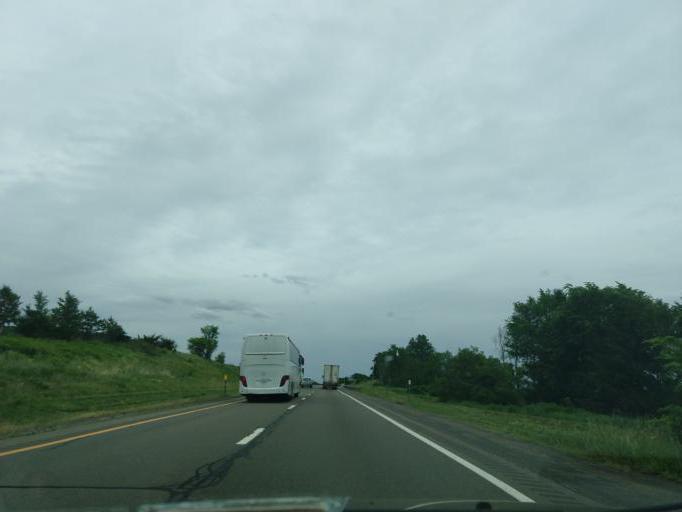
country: US
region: New York
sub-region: Chenango County
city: Lakeview
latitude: 42.4021
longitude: -76.0111
